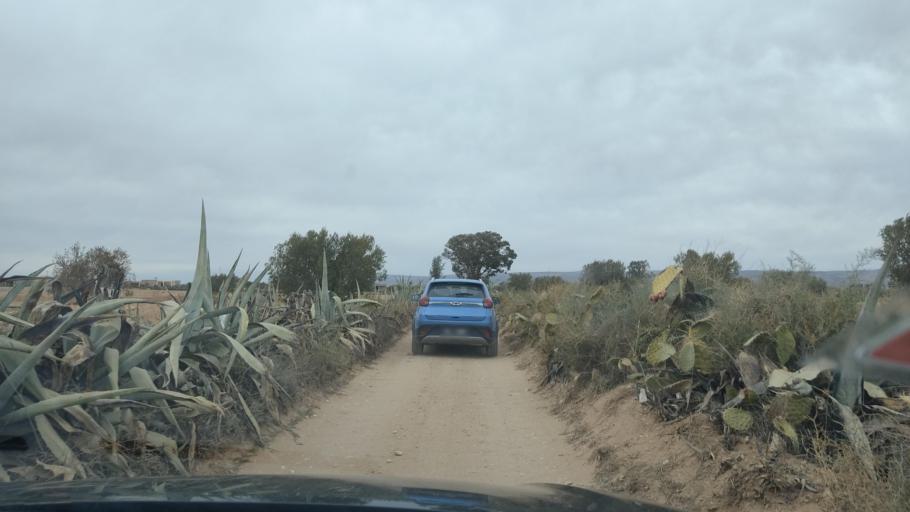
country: TN
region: Al Qasrayn
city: Kasserine
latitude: 35.2278
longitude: 8.9306
